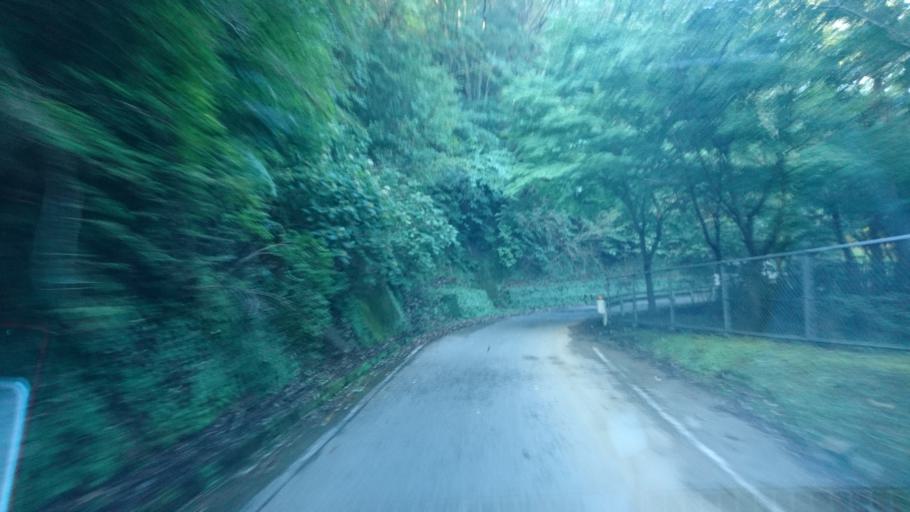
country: JP
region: Chiba
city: Kawaguchi
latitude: 35.1765
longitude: 140.0161
